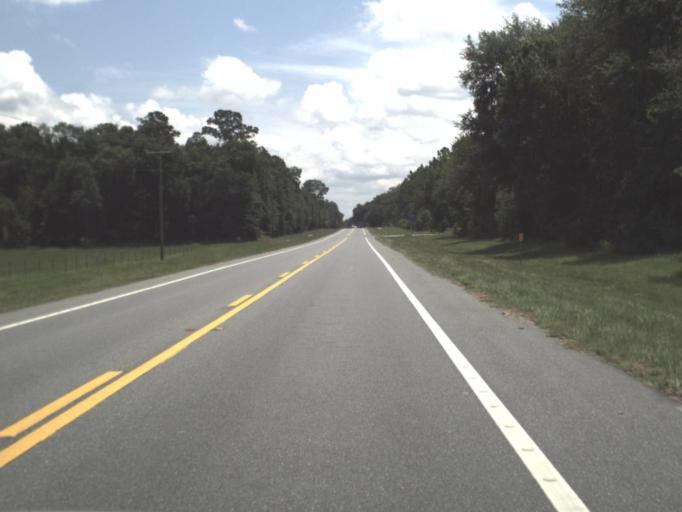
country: US
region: Florida
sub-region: Alachua County
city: High Springs
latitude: 30.0027
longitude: -82.5285
